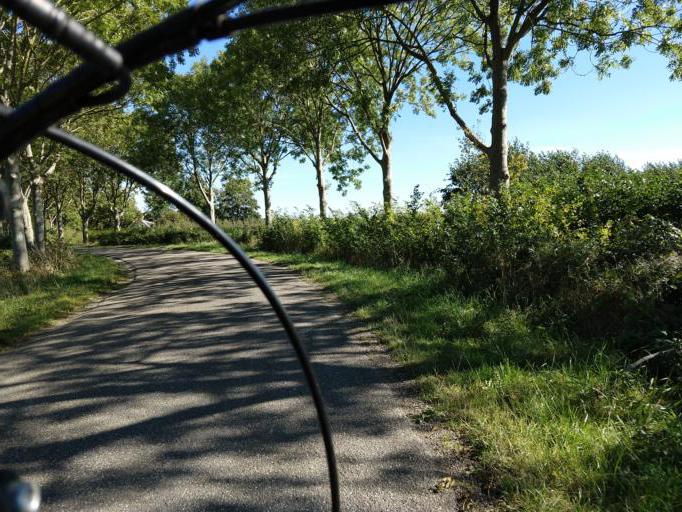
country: NL
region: Zeeland
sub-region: Gemeente Terneuzen
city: Terneuzen
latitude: 51.4115
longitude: 3.8329
